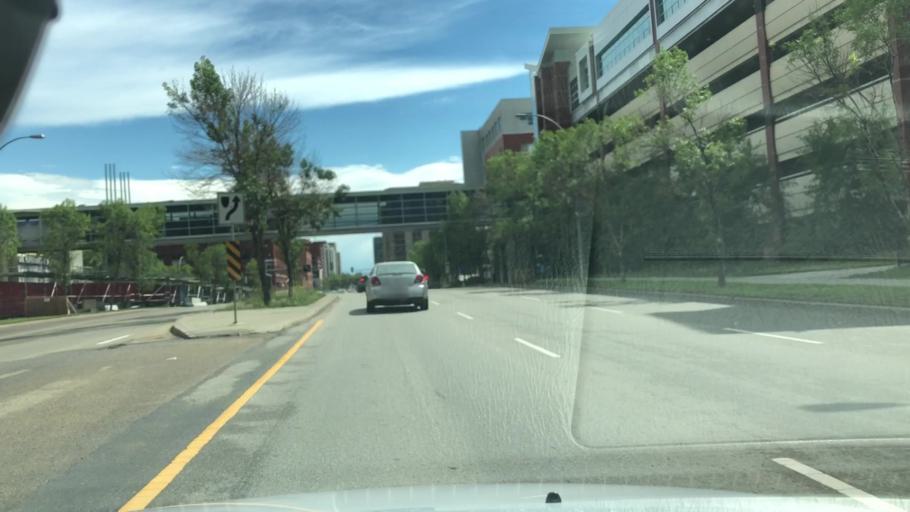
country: CA
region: Alberta
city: Edmonton
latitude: 53.5479
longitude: -113.5085
